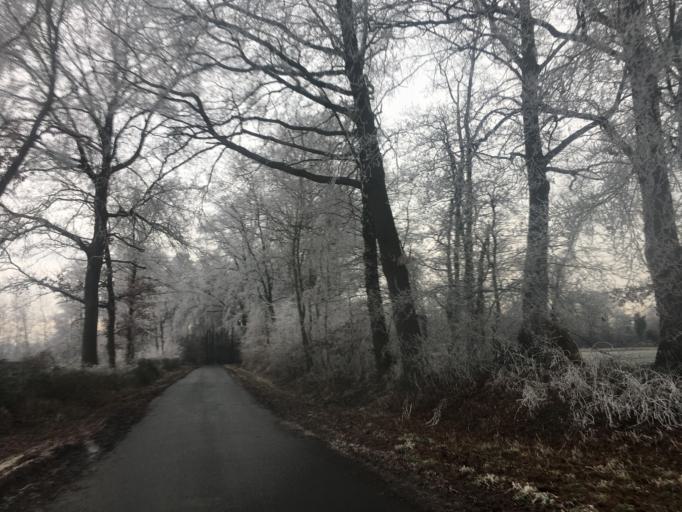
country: DE
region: North Rhine-Westphalia
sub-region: Regierungsbezirk Munster
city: Greven
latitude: 52.0802
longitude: 7.5577
